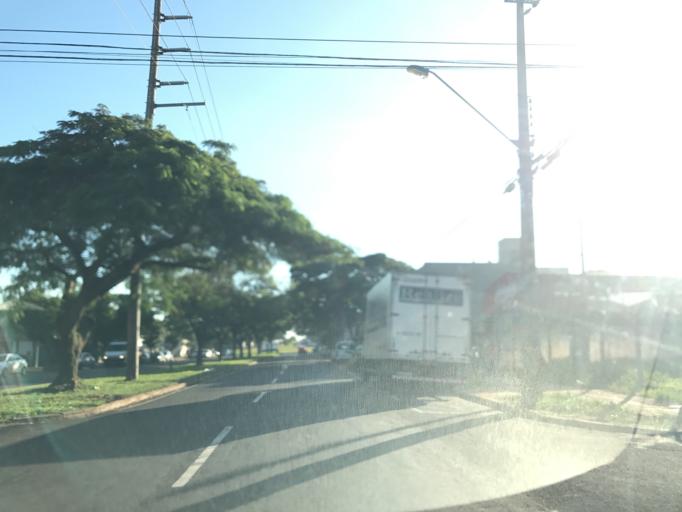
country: BR
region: Parana
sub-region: Maringa
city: Maringa
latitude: -23.4491
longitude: -51.9524
